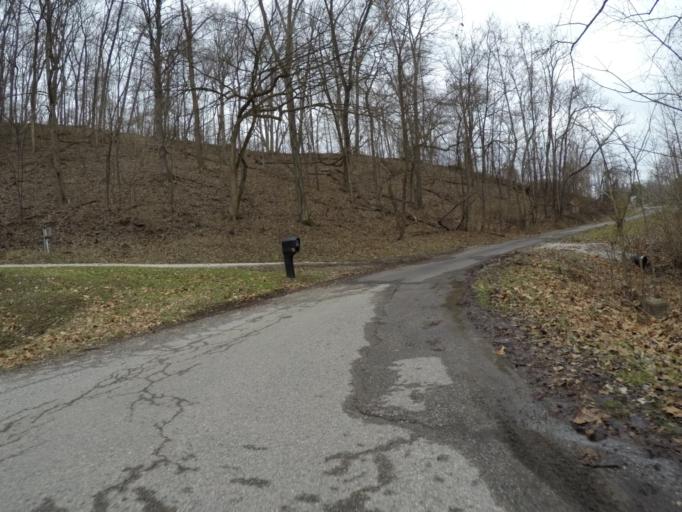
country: US
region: Ohio
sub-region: Lawrence County
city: Burlington
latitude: 38.3804
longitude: -82.5124
